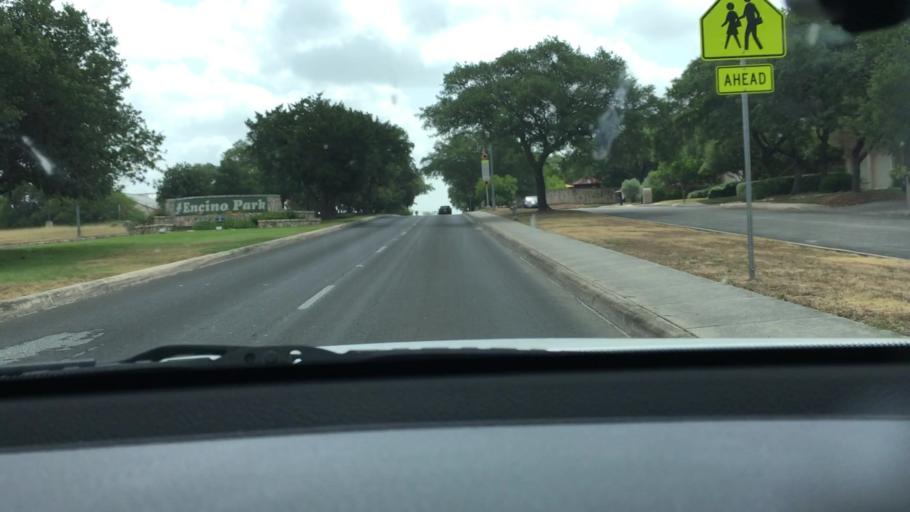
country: US
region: Texas
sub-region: Bexar County
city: Hollywood Park
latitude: 29.6301
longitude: -98.4565
